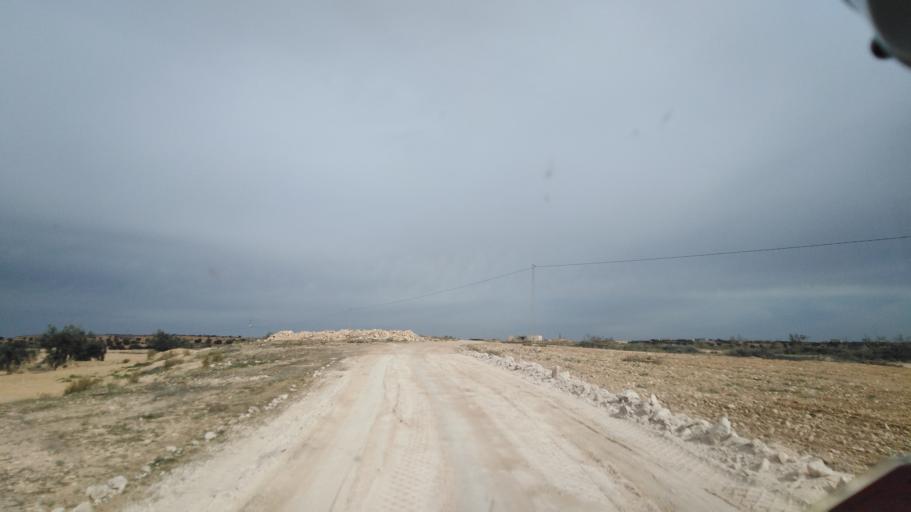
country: TN
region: Safaqis
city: Bi'r `Ali Bin Khalifah
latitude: 34.8166
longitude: 10.3073
